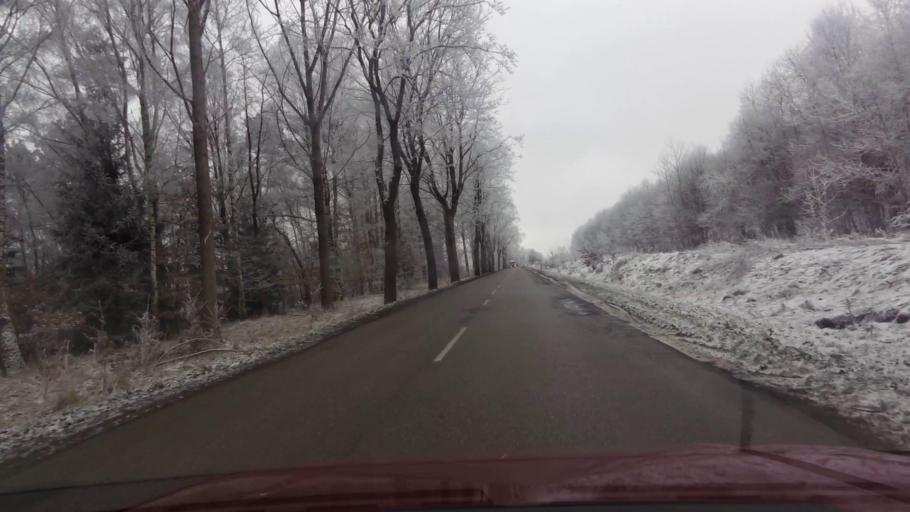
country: PL
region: West Pomeranian Voivodeship
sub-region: Powiat swidwinski
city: Polczyn-Zdroj
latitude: 53.7901
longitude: 16.0163
